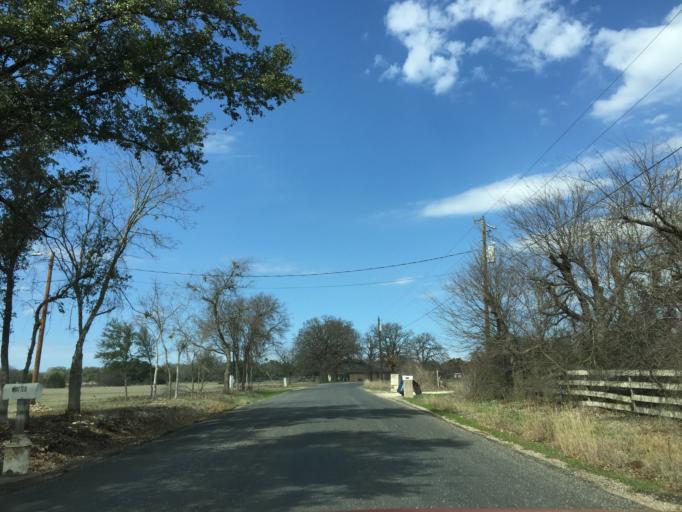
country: US
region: Texas
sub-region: Burnet County
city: Bertram
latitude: 30.7473
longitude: -97.9406
